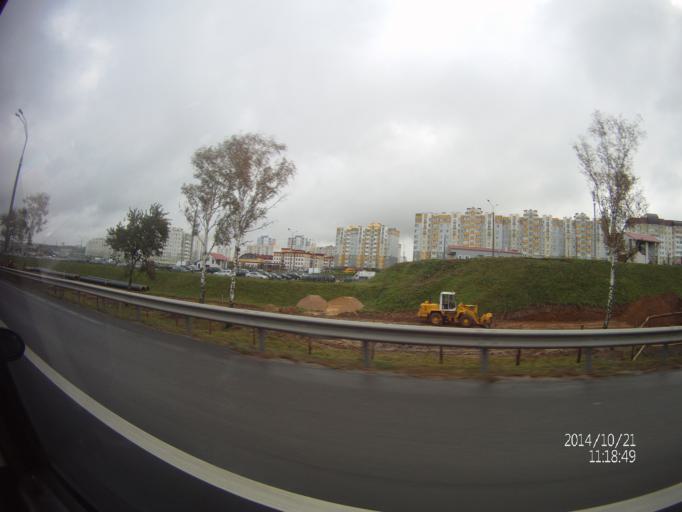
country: BY
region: Minsk
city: Novoye Medvezhino
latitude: 53.8873
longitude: 27.4142
